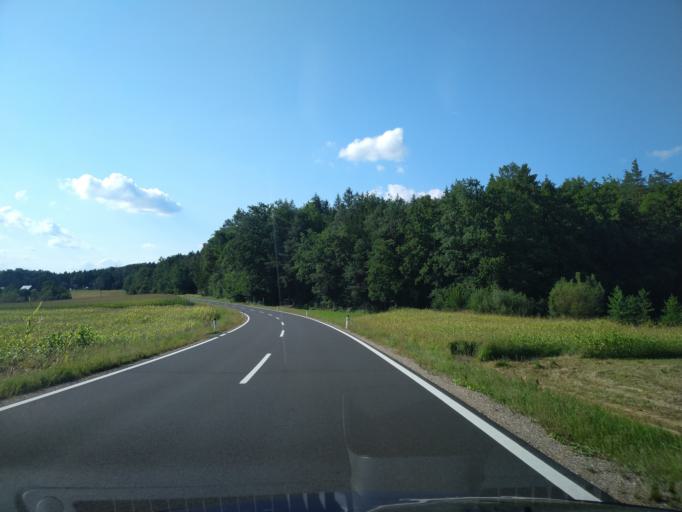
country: AT
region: Styria
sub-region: Politischer Bezirk Leibnitz
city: Sankt Johann im Saggautal
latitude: 46.7305
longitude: 15.3934
